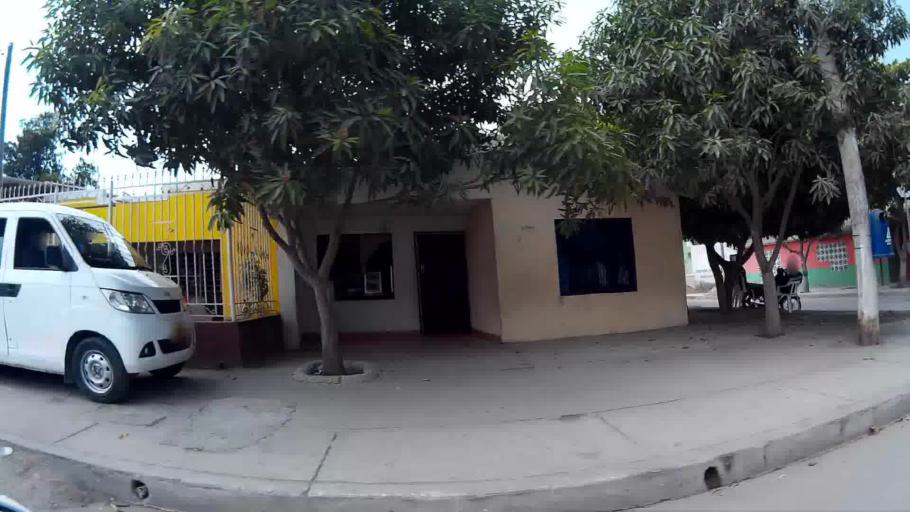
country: CO
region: Magdalena
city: Cienaga
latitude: 11.0061
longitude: -74.2430
